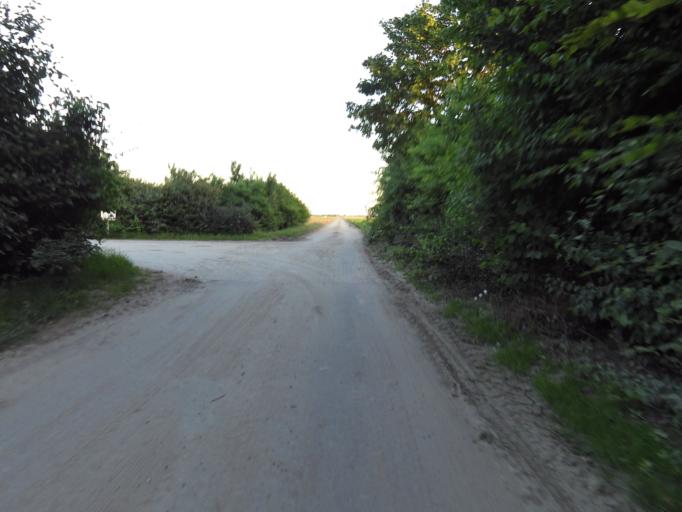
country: DE
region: Rheinland-Pfalz
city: Bobenheim-Roxheim
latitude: 49.5750
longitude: 8.3467
